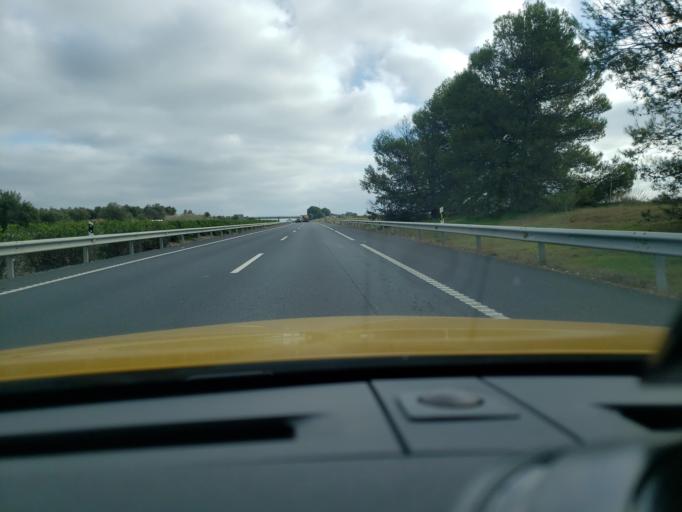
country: ES
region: Andalusia
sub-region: Provincia de Huelva
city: Chucena
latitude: 37.3535
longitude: -6.3777
